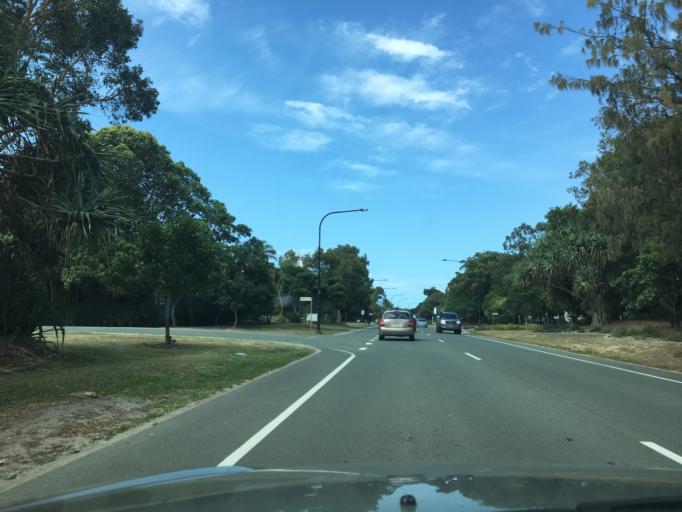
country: AU
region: Queensland
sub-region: Moreton Bay
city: Woorim
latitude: -27.0708
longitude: 153.2007
